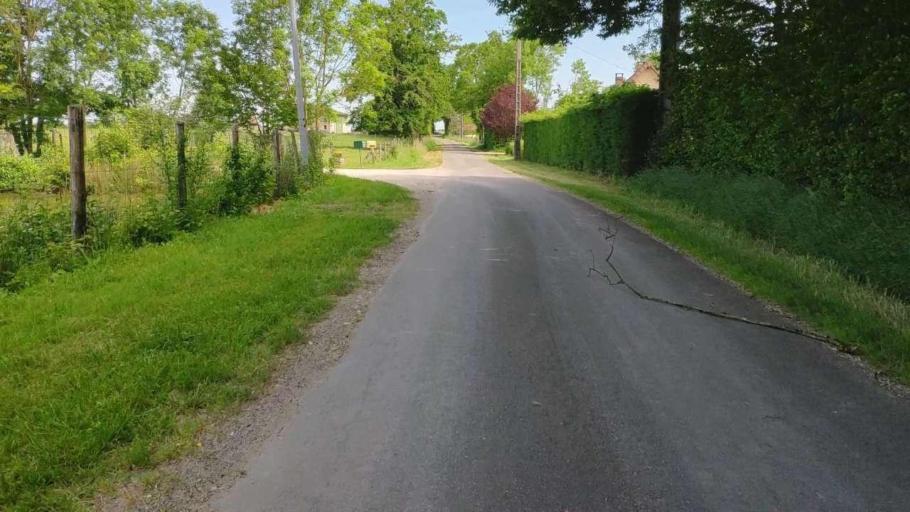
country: FR
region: Franche-Comte
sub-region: Departement du Jura
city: Bletterans
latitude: 46.6798
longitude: 5.4082
